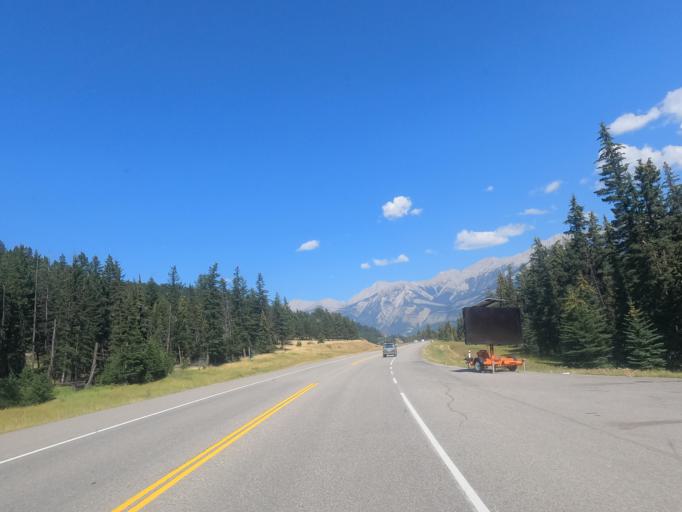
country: CA
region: Alberta
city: Jasper Park Lodge
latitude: 52.9046
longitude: -118.0646
